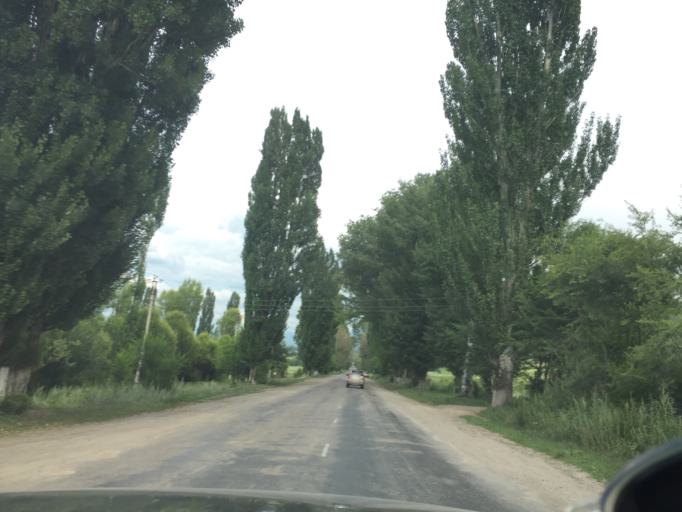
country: KG
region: Ysyk-Koel
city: Teploklyuchenka
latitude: 42.5168
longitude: 78.5956
